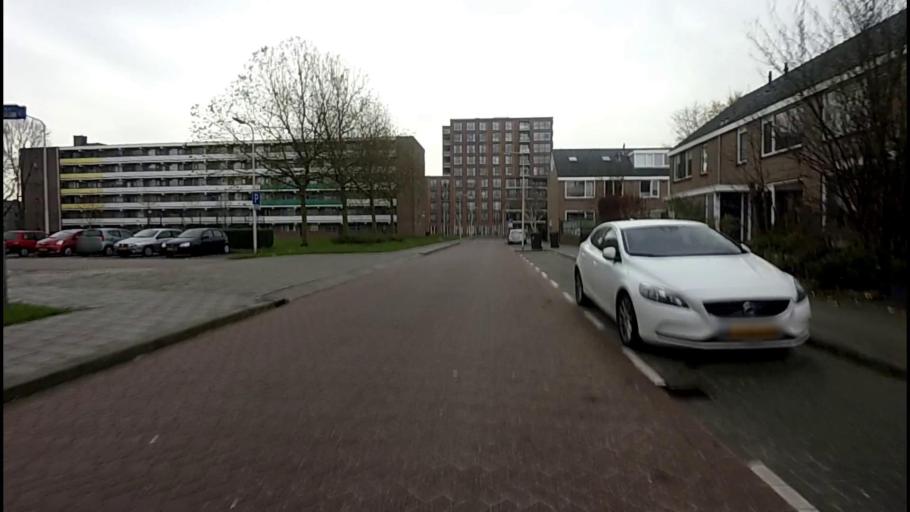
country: NL
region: South Holland
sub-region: Gemeente Gouda
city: Gouda
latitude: 52.0122
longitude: 4.7376
